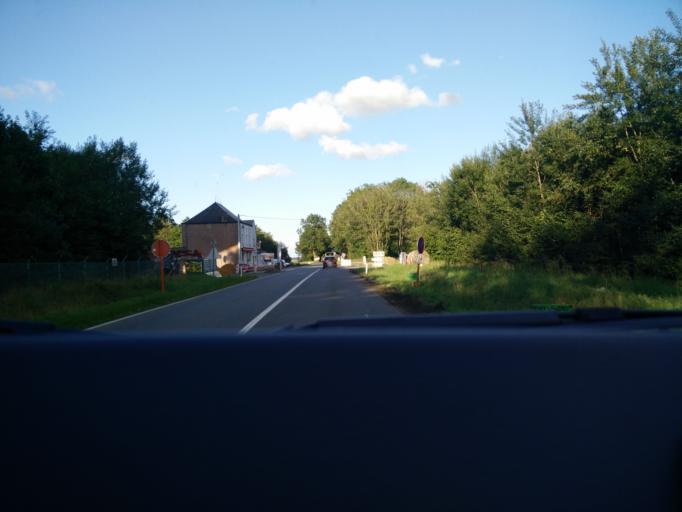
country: BE
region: Wallonia
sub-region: Province de Namur
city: Florennes
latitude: 50.2248
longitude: 4.6540
